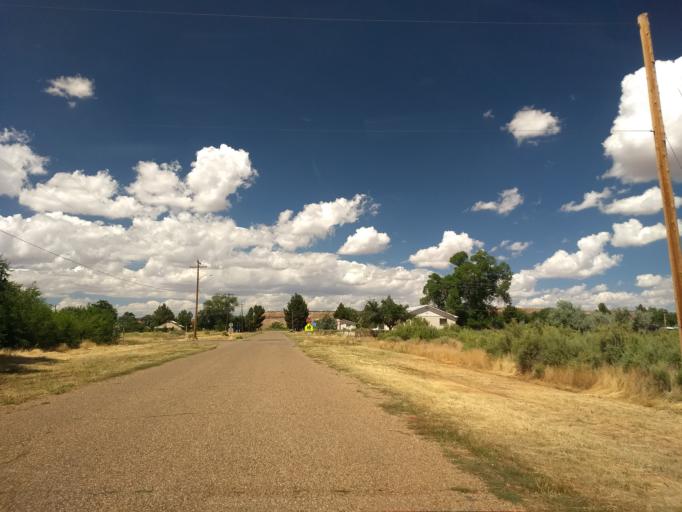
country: US
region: Arizona
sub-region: Coconino County
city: Fredonia
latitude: 36.9525
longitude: -112.5236
